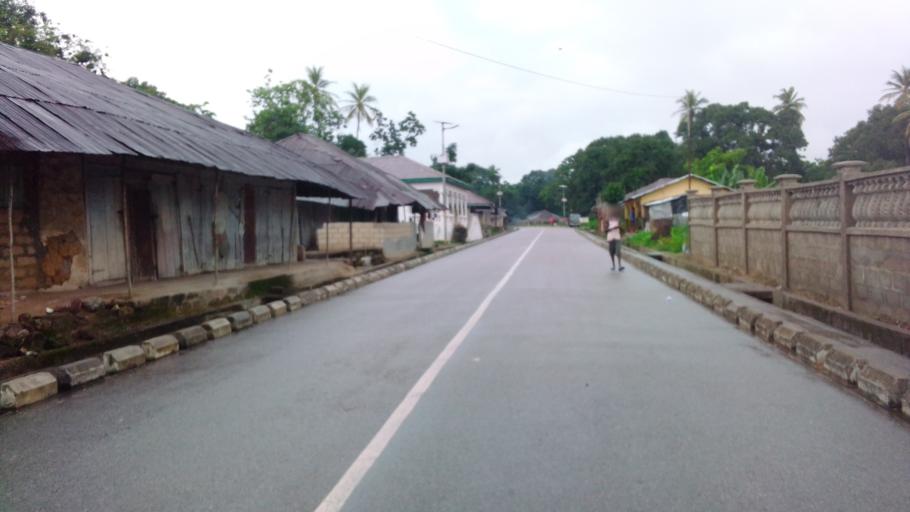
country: SL
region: Northern Province
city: Lunsar
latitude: 8.6797
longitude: -12.5323
